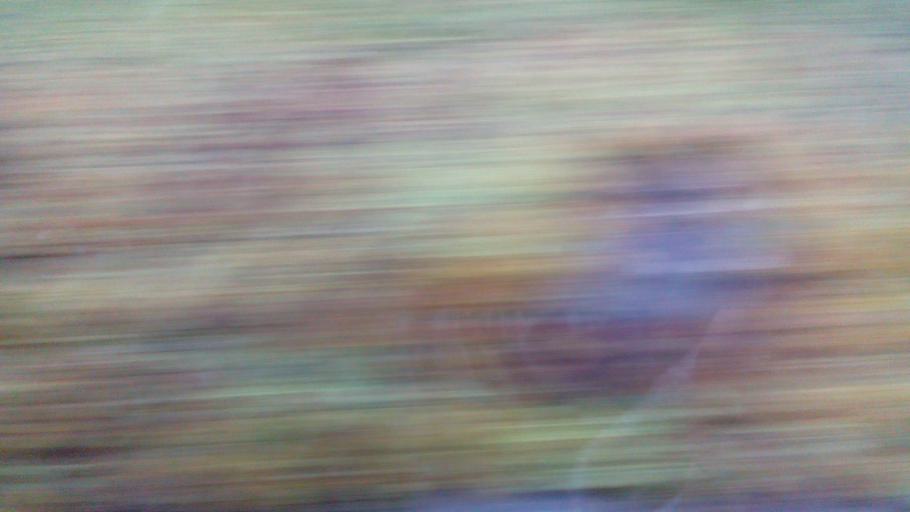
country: TW
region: Taiwan
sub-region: Hualien
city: Hualian
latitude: 24.3975
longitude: 121.3662
